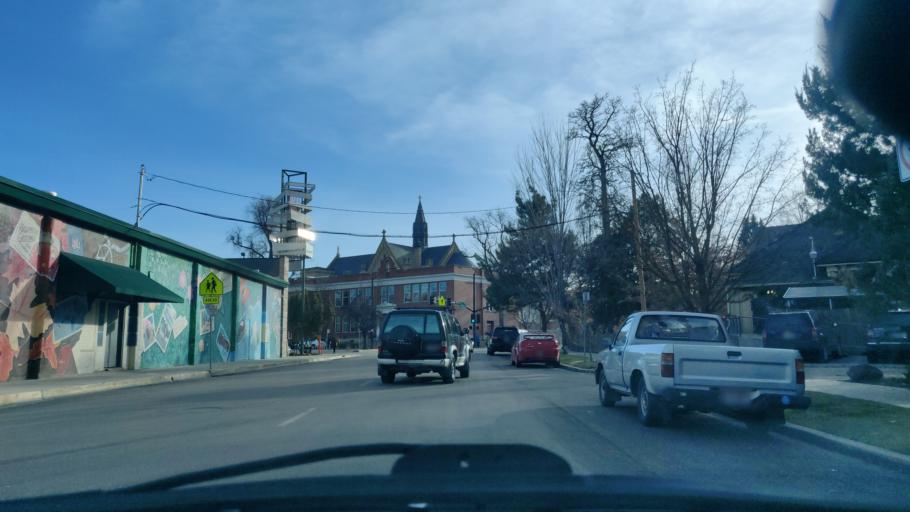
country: US
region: Idaho
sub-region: Ada County
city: Boise
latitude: 43.6231
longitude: -116.1987
